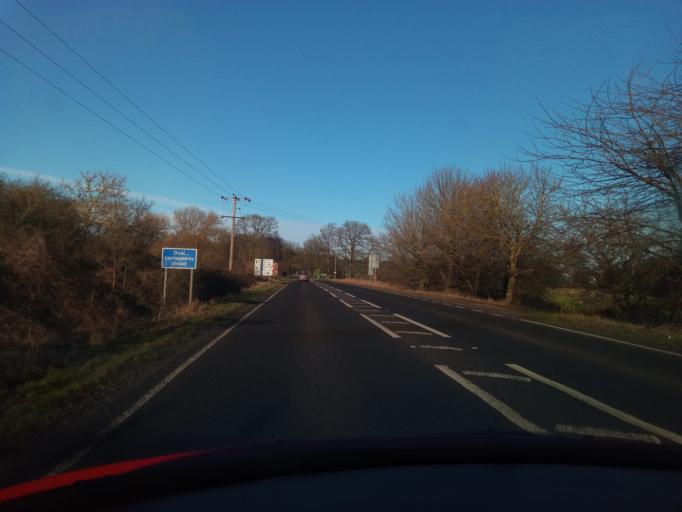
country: GB
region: England
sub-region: Nottinghamshire
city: Farnsfield
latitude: 53.0506
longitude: -1.0669
